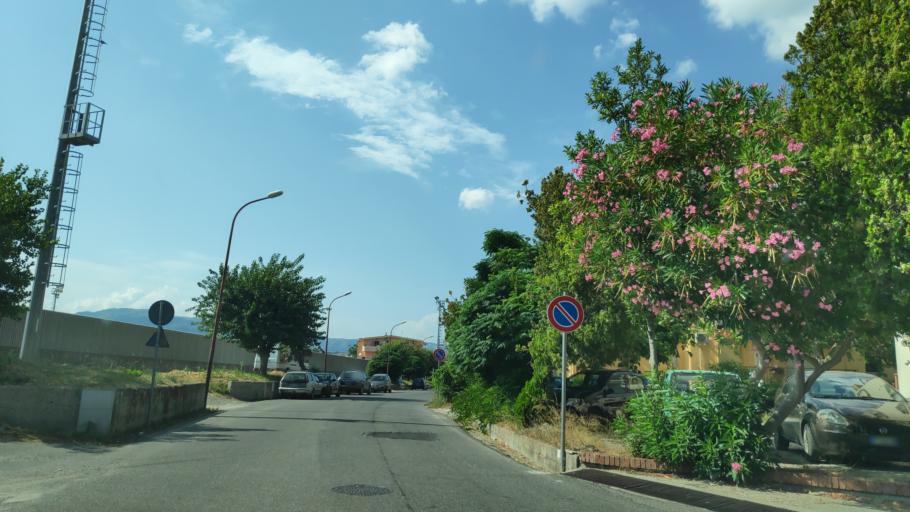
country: IT
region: Calabria
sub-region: Provincia di Catanzaro
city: Marina di Davoli
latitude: 38.6621
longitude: 16.5431
